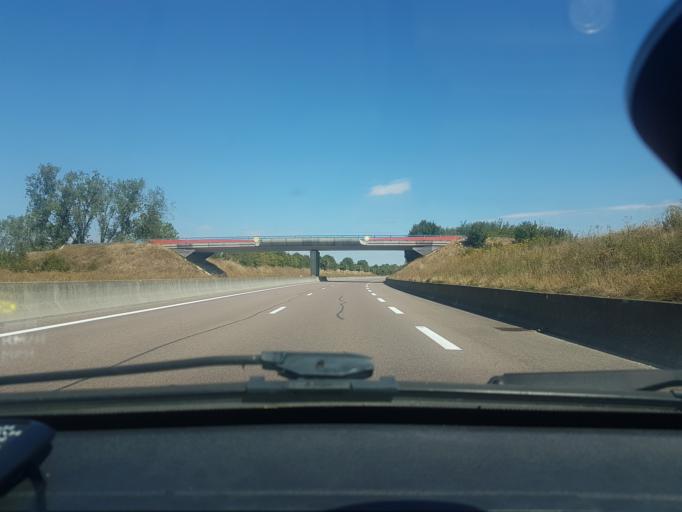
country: FR
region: Bourgogne
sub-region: Departement de la Cote-d'Or
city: Quetigny
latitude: 47.3323
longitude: 5.1076
